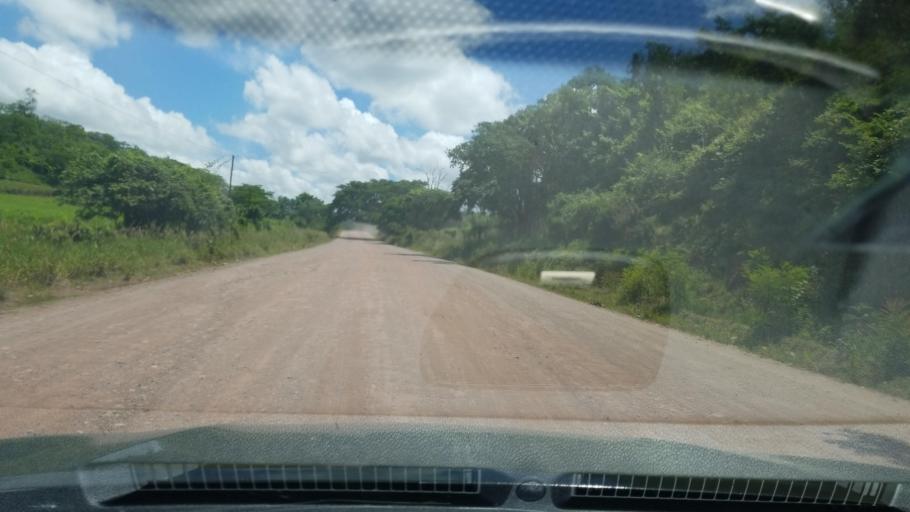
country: HN
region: Francisco Morazan
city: San Juan de Flores
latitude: 14.3242
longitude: -87.0469
